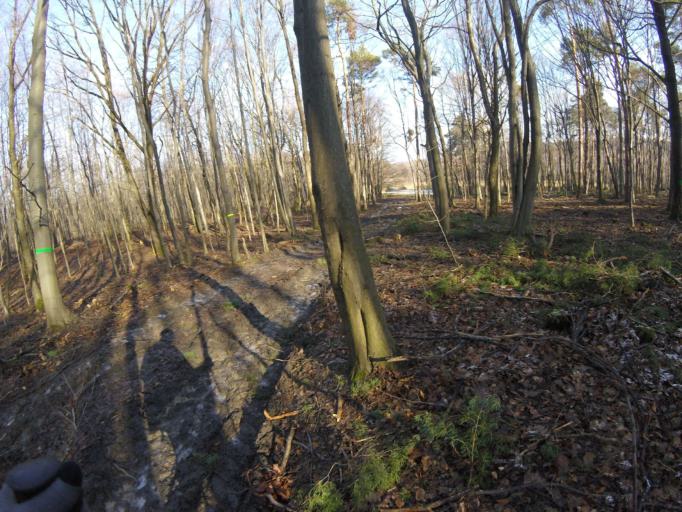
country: HU
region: Komarom-Esztergom
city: Pilismarot
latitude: 47.7476
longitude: 18.8835
